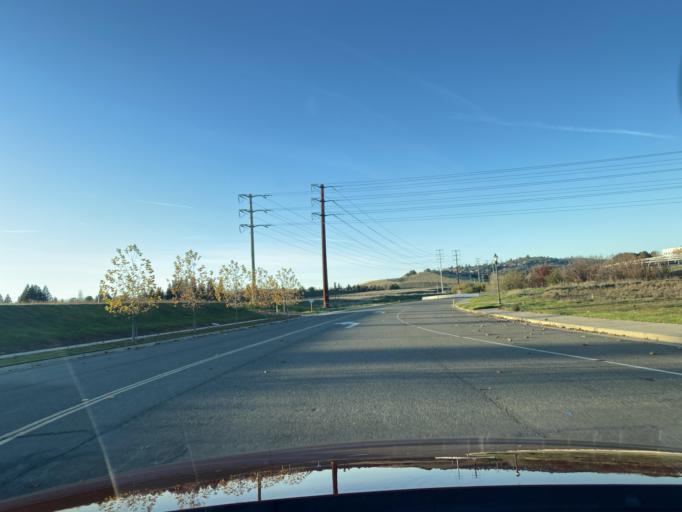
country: US
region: California
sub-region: El Dorado County
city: El Dorado Hills
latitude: 38.6446
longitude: -121.0718
